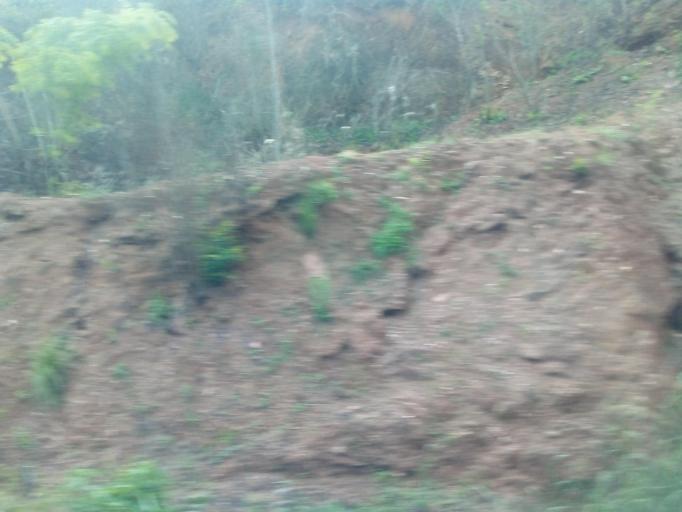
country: BR
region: Minas Gerais
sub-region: Caete
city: Caete
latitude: -19.9097
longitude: -43.6982
